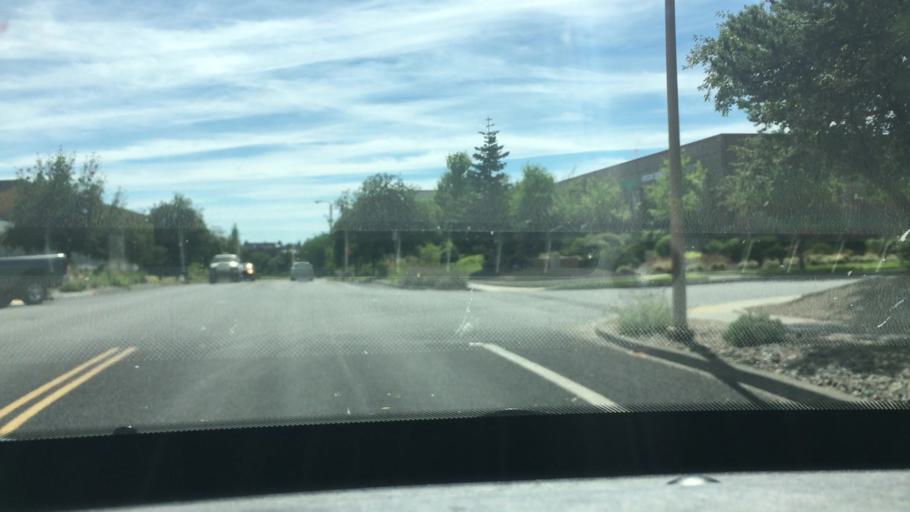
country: US
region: Oregon
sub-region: Deschutes County
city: Bend
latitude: 44.0480
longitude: -121.3253
